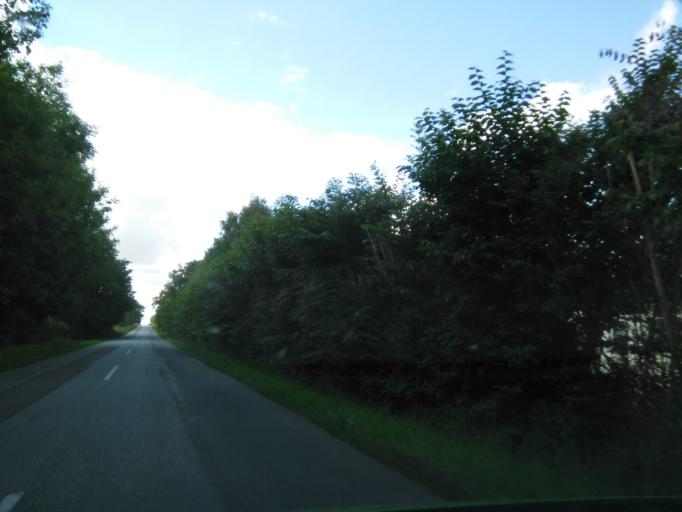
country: DK
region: Central Jutland
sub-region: Arhus Kommune
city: Solbjerg
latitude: 56.0626
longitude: 10.0931
